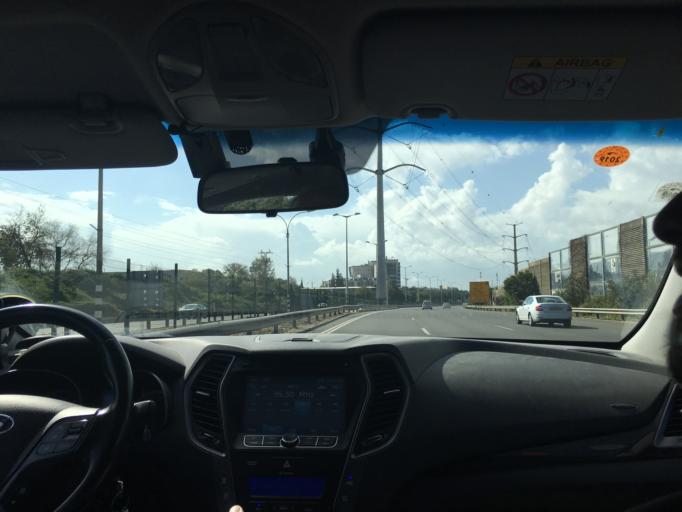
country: IL
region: Tel Aviv
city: Giv`at Shemu'el
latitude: 32.0733
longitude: 34.8434
